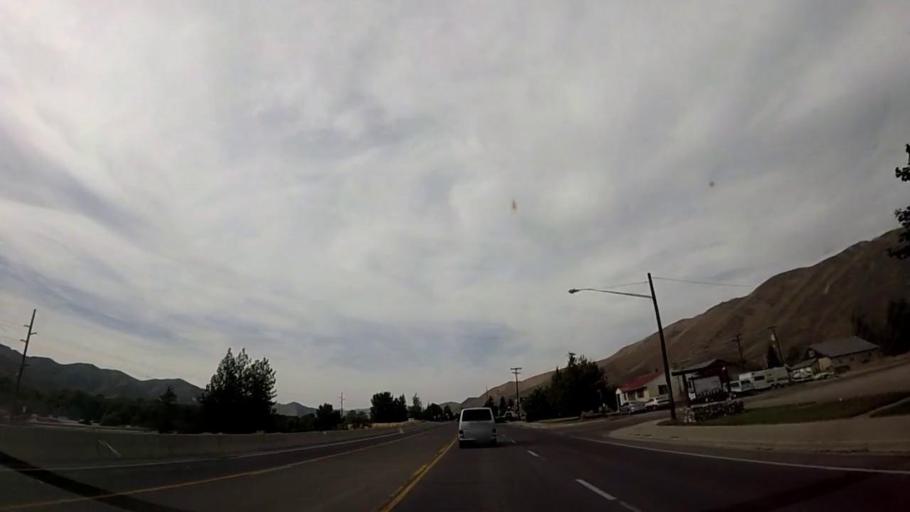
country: US
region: Idaho
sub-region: Blaine County
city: Bellevue
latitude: 43.4684
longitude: -114.2626
